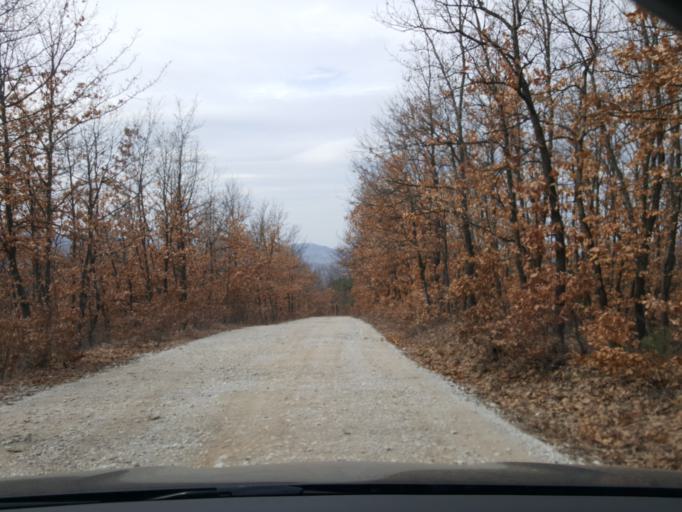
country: RS
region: Central Serbia
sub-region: Pirotski Okrug
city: Dimitrovgrad
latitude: 43.0035
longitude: 22.7472
